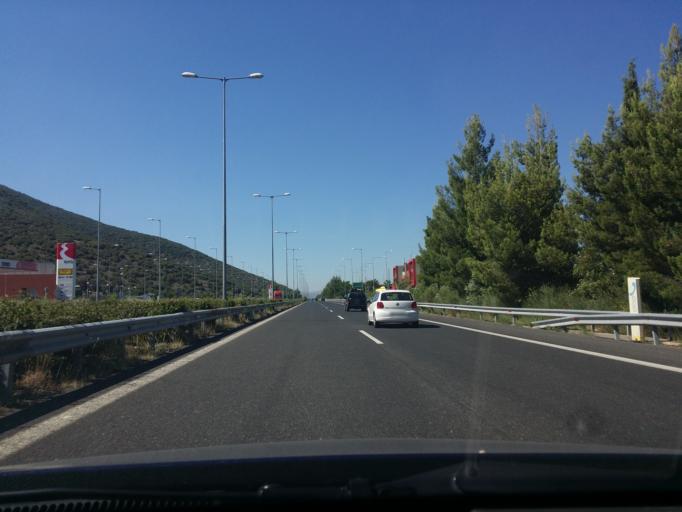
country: GR
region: Peloponnese
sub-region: Nomos Arkadias
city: Tripoli
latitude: 37.5817
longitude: 22.4322
